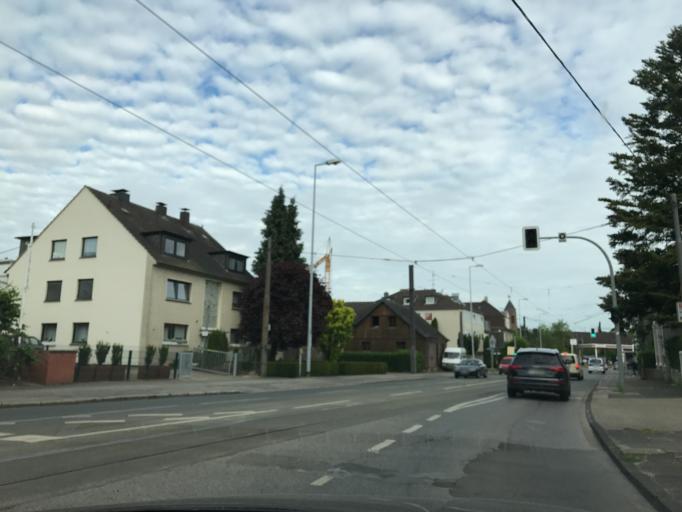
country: DE
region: North Rhine-Westphalia
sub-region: Regierungsbezirk Dusseldorf
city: Muelheim (Ruhr)
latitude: 51.4157
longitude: 6.9070
